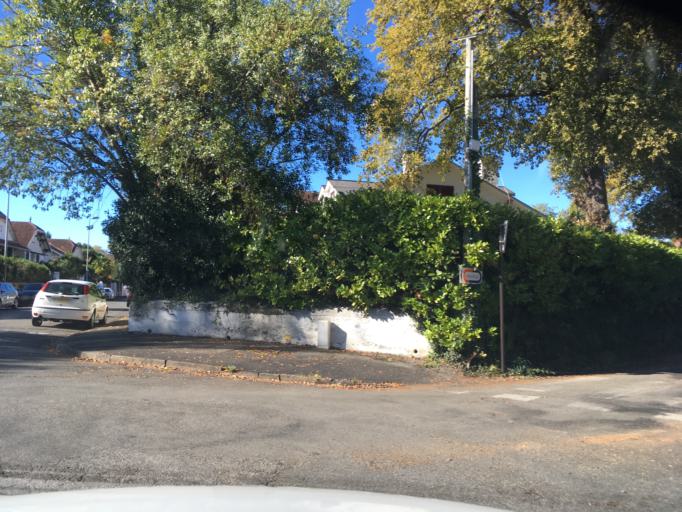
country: FR
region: Aquitaine
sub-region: Departement des Pyrenees-Atlantiques
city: Bizanos
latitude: 43.3018
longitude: -0.3448
